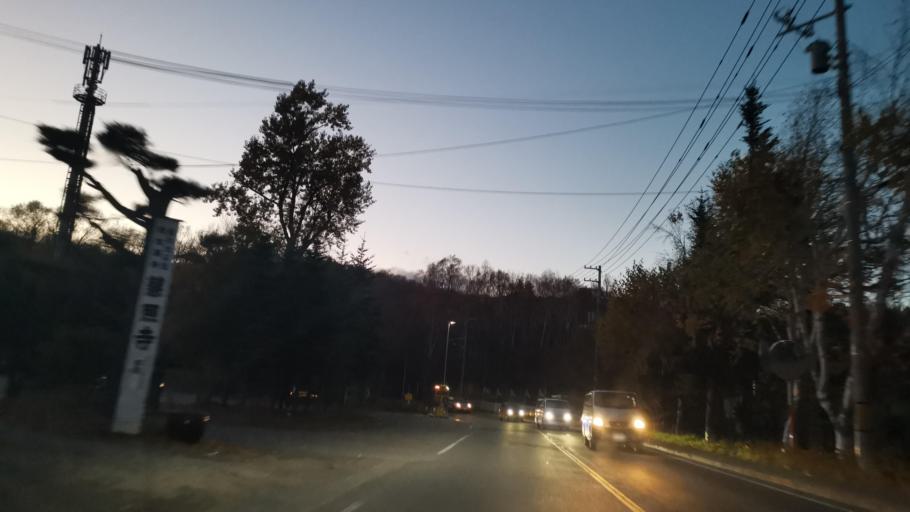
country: JP
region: Hokkaido
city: Sapporo
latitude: 42.9948
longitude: 141.3649
